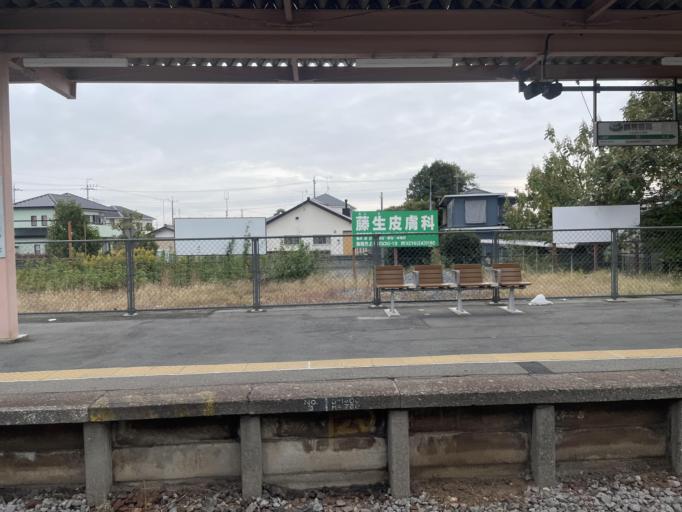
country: JP
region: Gunma
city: Fujioka
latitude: 36.2502
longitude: 139.0835
